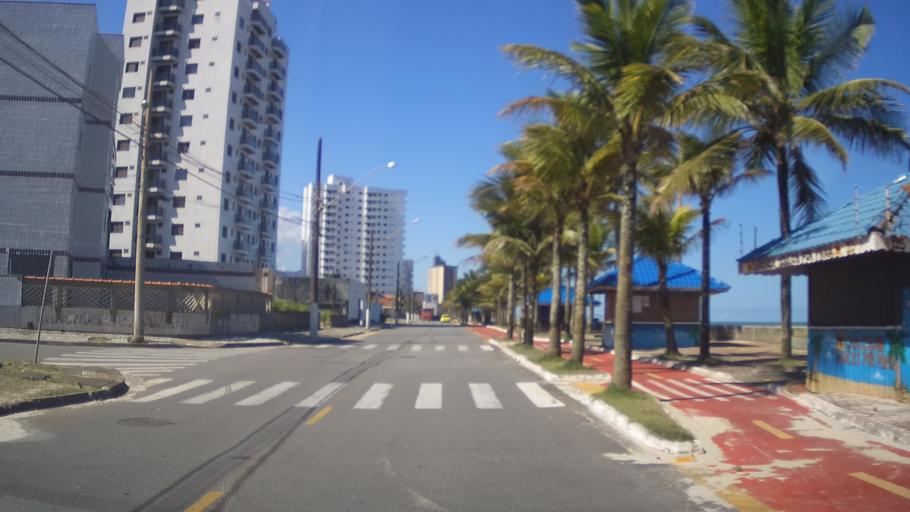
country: BR
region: Sao Paulo
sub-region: Mongagua
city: Mongagua
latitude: -24.1186
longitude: -46.6645
